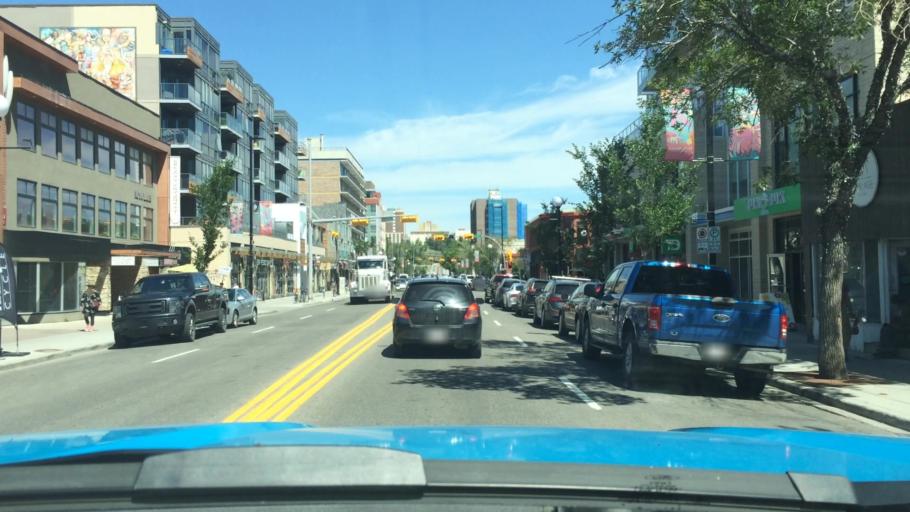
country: CA
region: Alberta
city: Calgary
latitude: 51.0534
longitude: -114.0859
